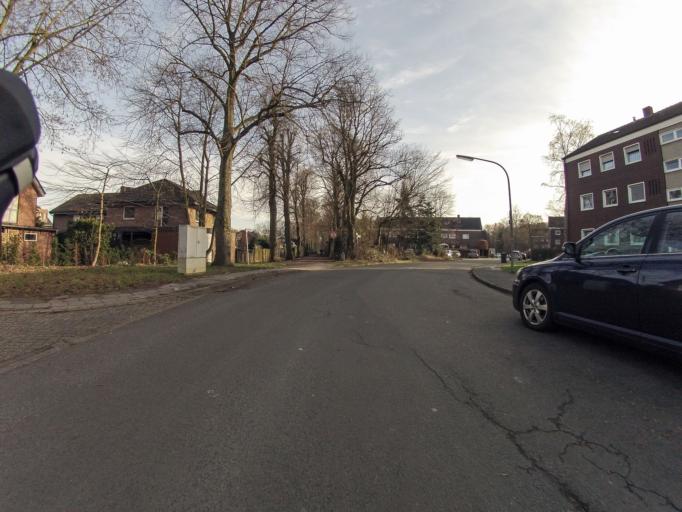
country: DE
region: North Rhine-Westphalia
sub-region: Regierungsbezirk Munster
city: Rheine
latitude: 52.2669
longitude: 7.4501
